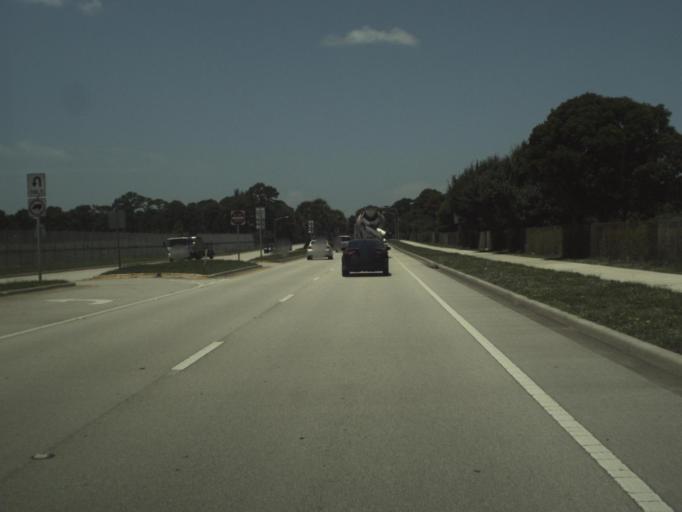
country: US
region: Florida
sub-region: Martin County
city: Stuart
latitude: 27.1836
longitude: -80.2320
